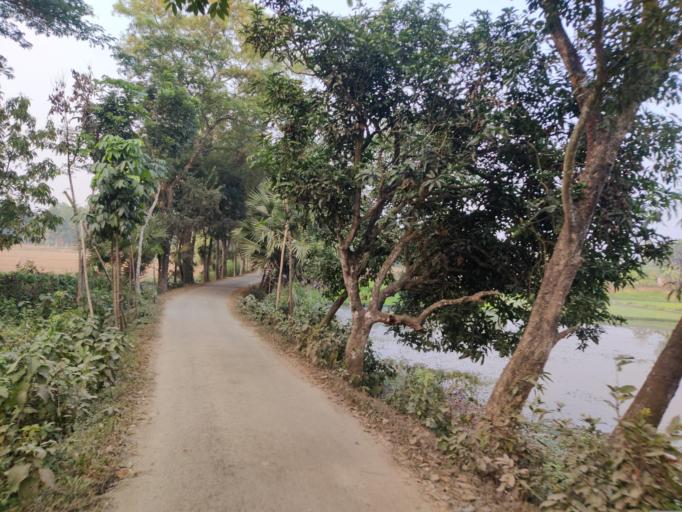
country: BD
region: Dhaka
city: Bajitpur
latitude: 24.1554
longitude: 90.7616
